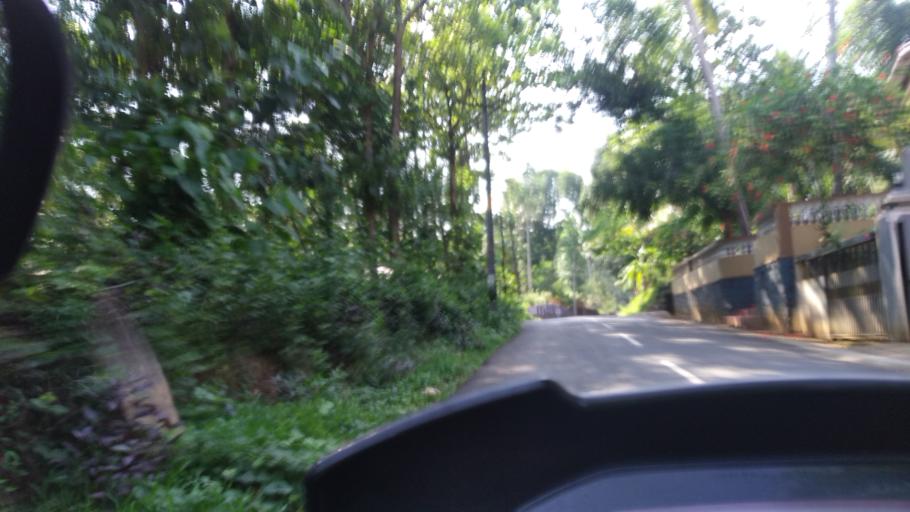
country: IN
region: Kerala
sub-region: Kottayam
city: Palackattumala
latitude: 9.8012
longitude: 76.5824
